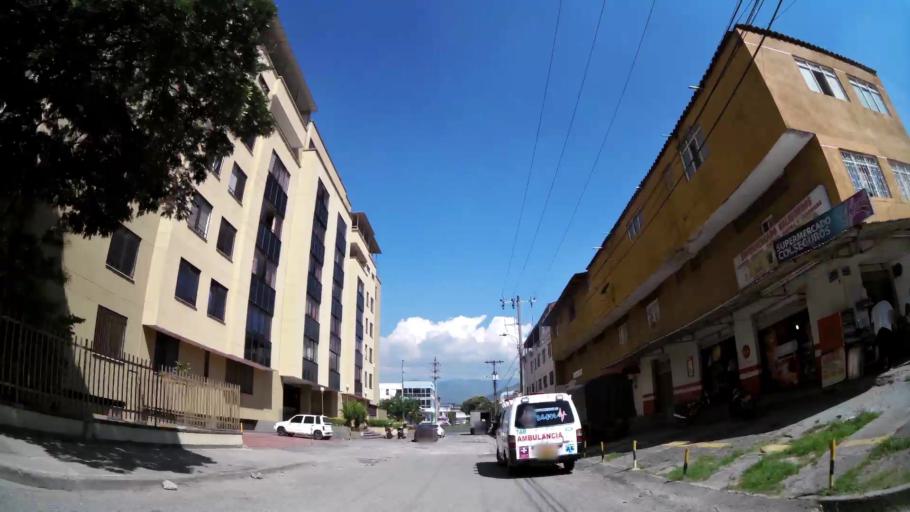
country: CO
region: Valle del Cauca
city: Cali
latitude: 3.4299
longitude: -76.5290
